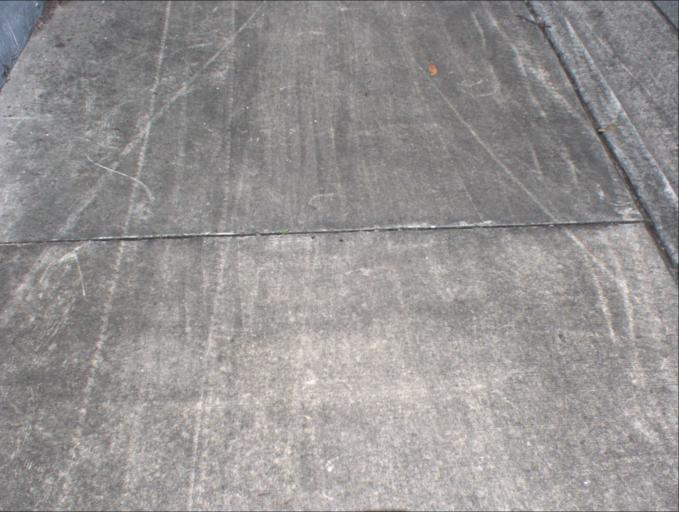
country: AU
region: Queensland
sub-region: Logan
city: Park Ridge South
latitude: -27.7241
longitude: 153.0311
